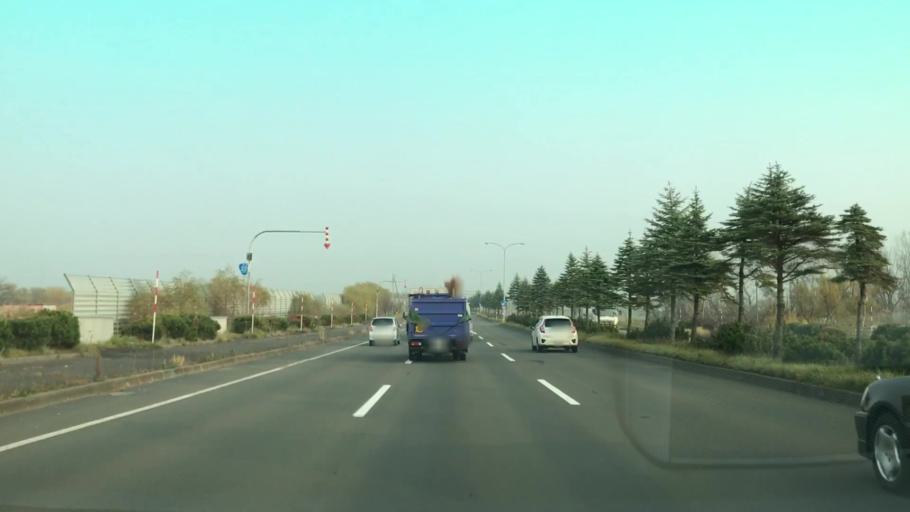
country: JP
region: Hokkaido
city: Ishikari
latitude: 43.1698
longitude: 141.3485
